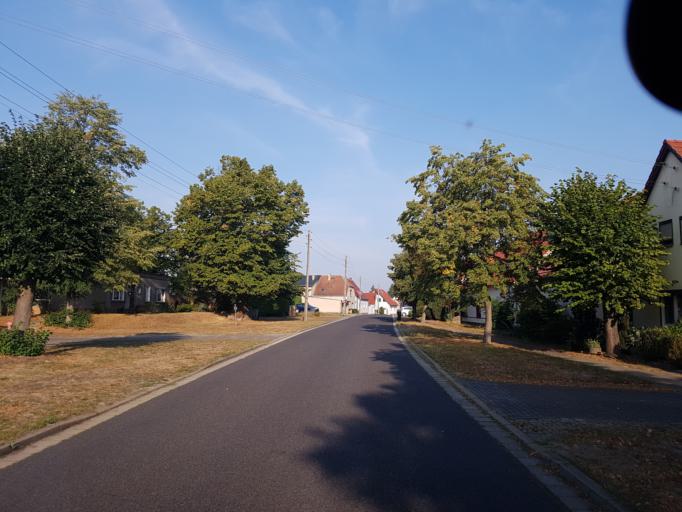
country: DE
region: Brandenburg
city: Finsterwalde
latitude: 51.6662
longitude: 13.7325
